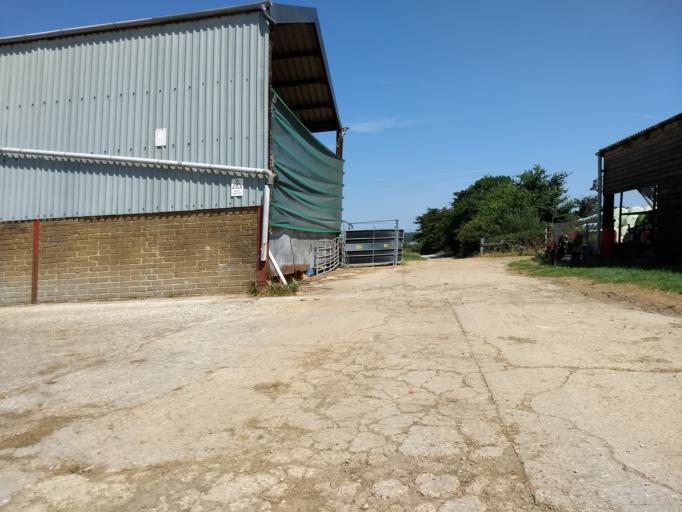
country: GB
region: England
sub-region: Isle of Wight
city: Newport
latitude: 50.6953
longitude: -1.3400
